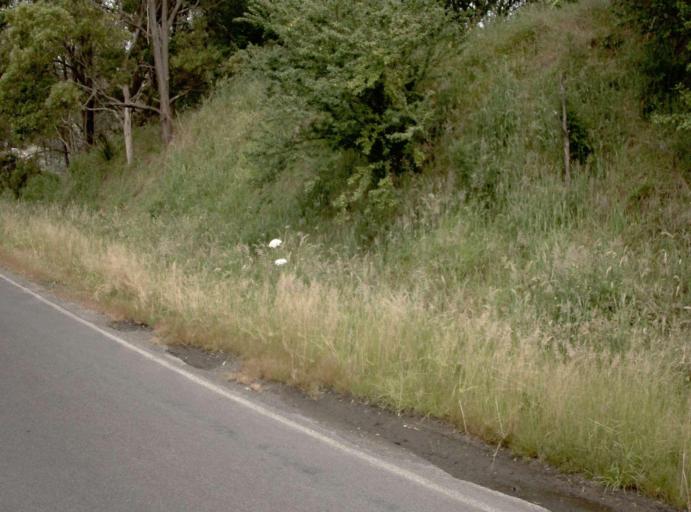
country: AU
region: Victoria
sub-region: Bass Coast
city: North Wonthaggi
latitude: -38.5196
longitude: 145.7020
